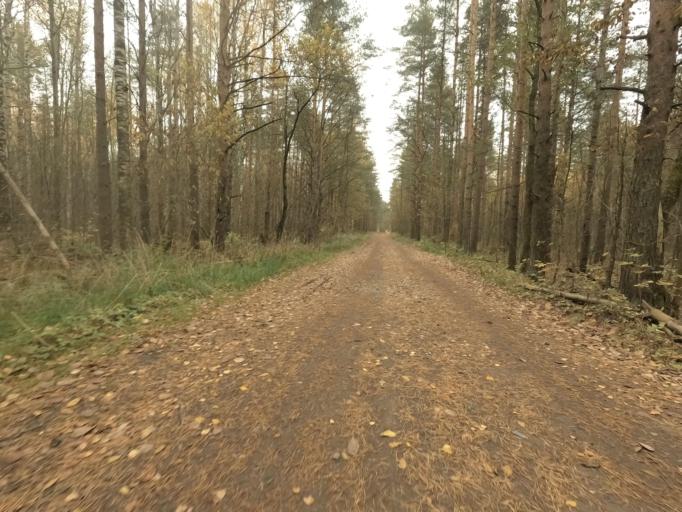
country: RU
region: Leningrad
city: Kirovsk
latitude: 59.8514
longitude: 30.9799
